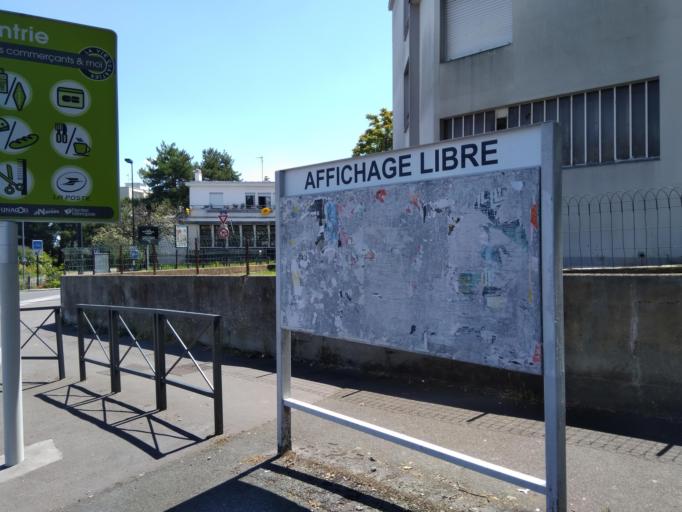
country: FR
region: Pays de la Loire
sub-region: Departement de la Loire-Atlantique
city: Nantes
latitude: 47.2216
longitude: -1.5929
